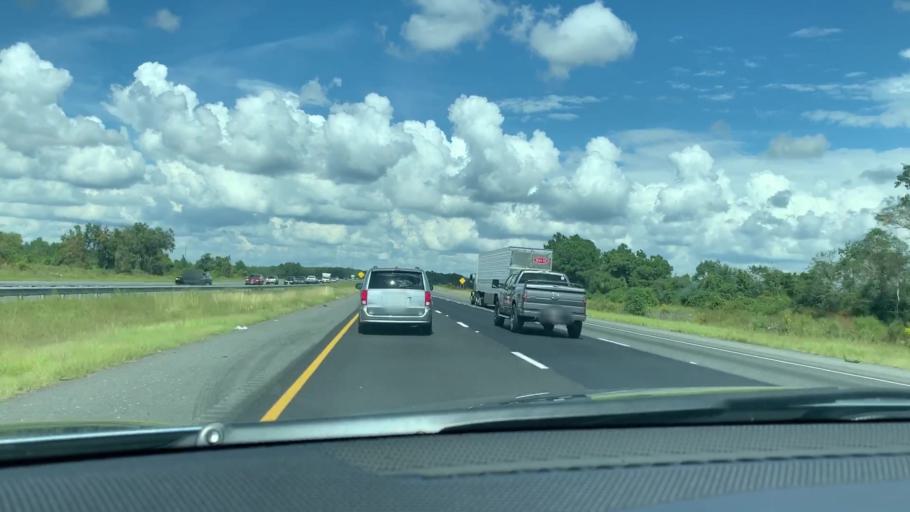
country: US
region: Georgia
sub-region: Camden County
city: Woodbine
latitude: 31.0322
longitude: -81.6542
